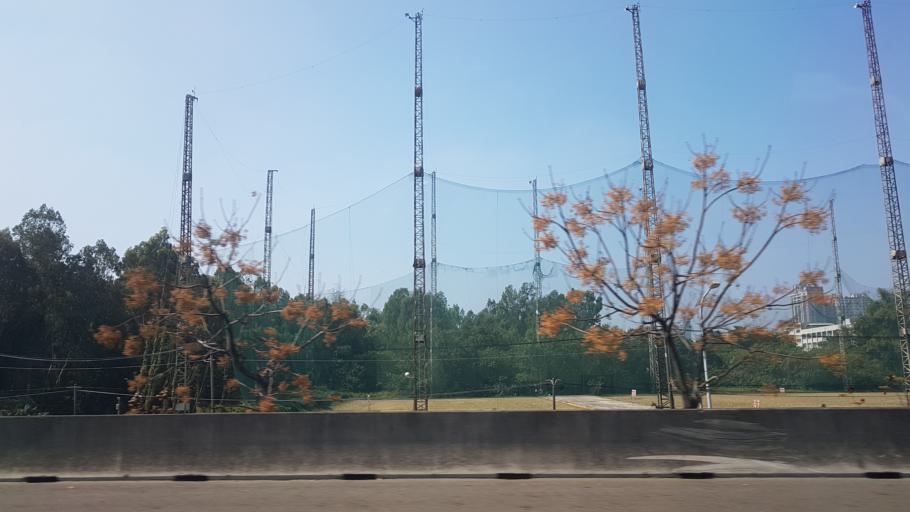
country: TW
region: Taiwan
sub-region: Tainan
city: Tainan
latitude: 22.9952
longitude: 120.2481
